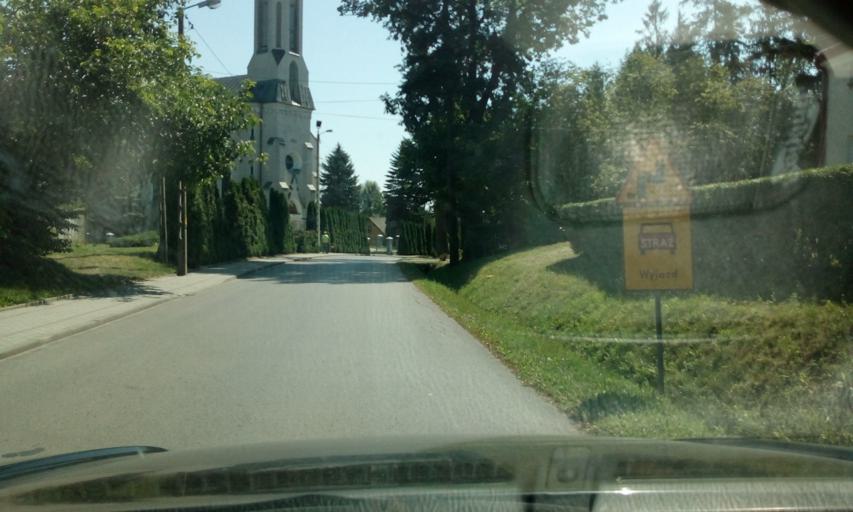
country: PL
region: Subcarpathian Voivodeship
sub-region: Powiat lancucki
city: Wysoka
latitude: 50.0453
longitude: 22.2487
